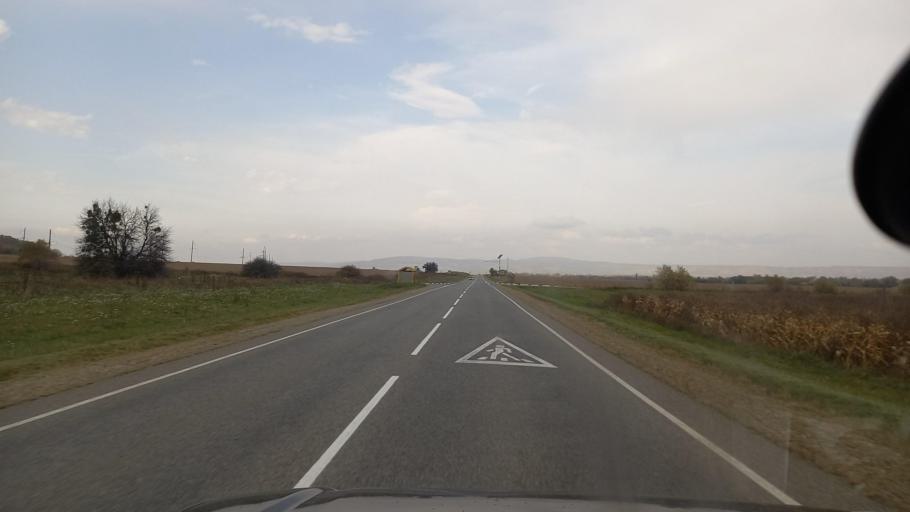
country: RU
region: Krasnodarskiy
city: Shedok
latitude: 44.2474
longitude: 40.8631
